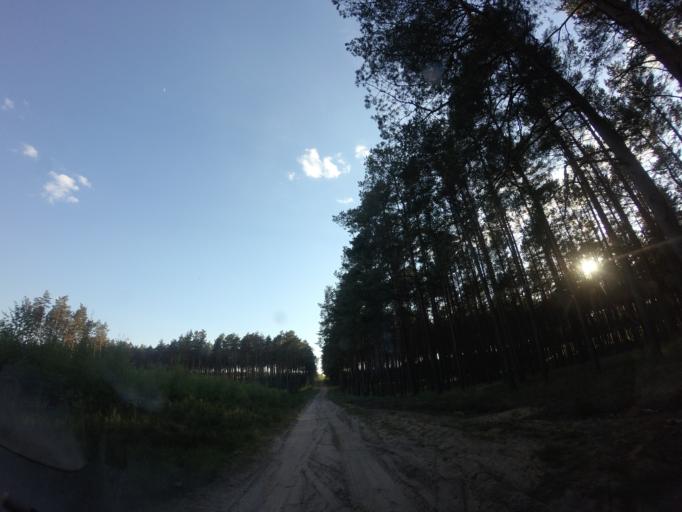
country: PL
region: West Pomeranian Voivodeship
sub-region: Powiat choszczenski
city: Drawno
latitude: 53.1576
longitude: 15.7317
